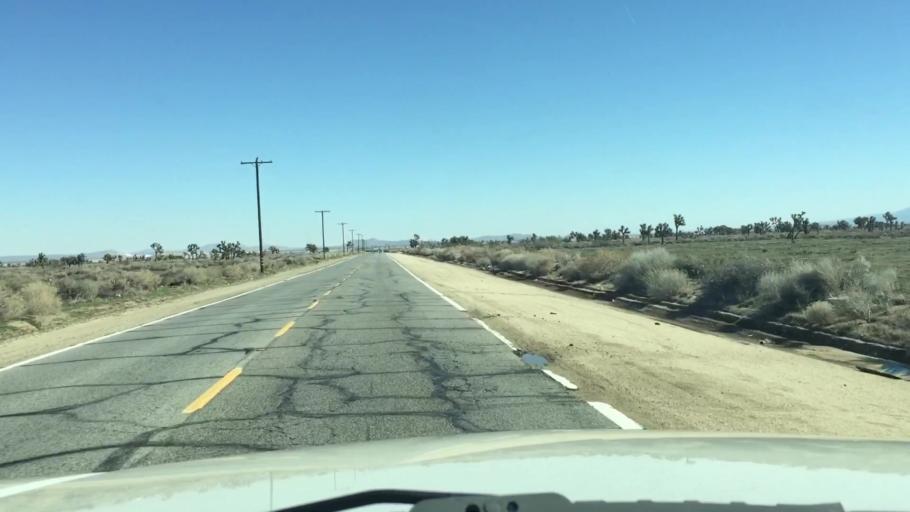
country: US
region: California
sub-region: Los Angeles County
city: Desert View Highlands
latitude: 34.6311
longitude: -118.1366
